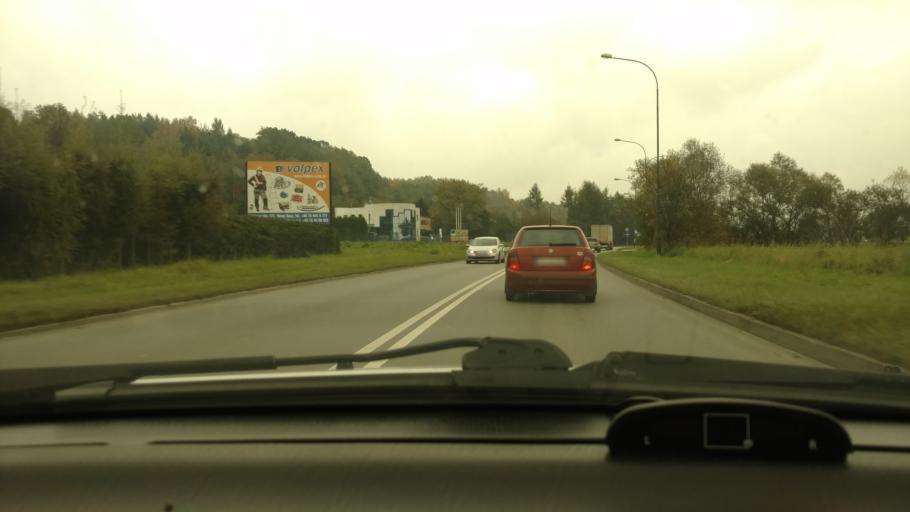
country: PL
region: Lesser Poland Voivodeship
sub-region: Powiat nowosadecki
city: Nowy Sacz
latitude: 49.6372
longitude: 20.7010
